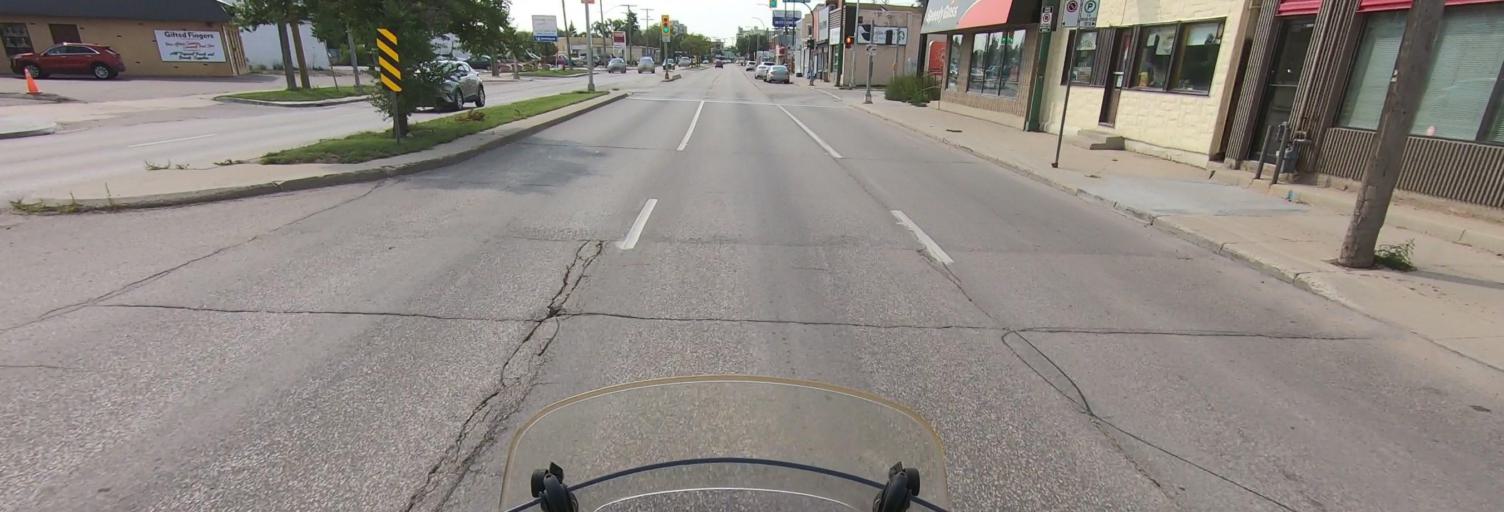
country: CA
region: Manitoba
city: Winnipeg
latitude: 49.8432
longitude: -97.1128
